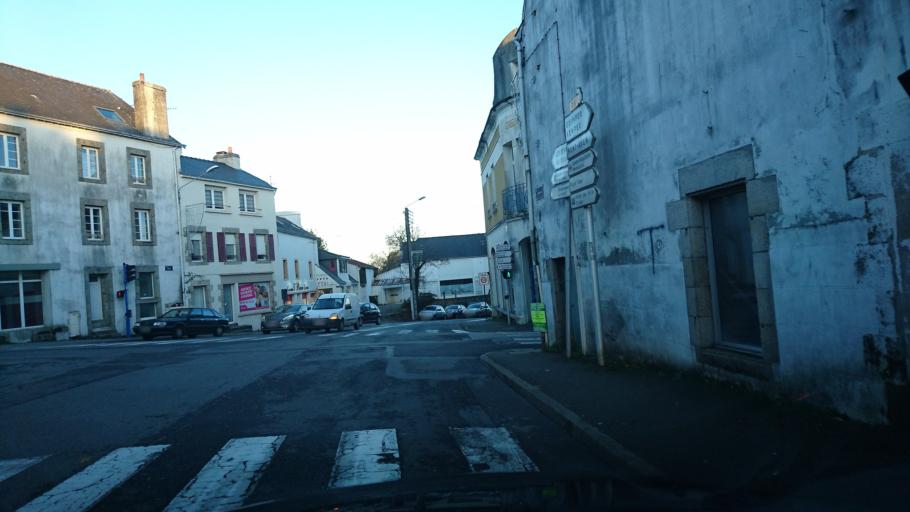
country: FR
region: Brittany
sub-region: Departement du Finistere
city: Quimperle
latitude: 47.8738
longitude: -3.5502
